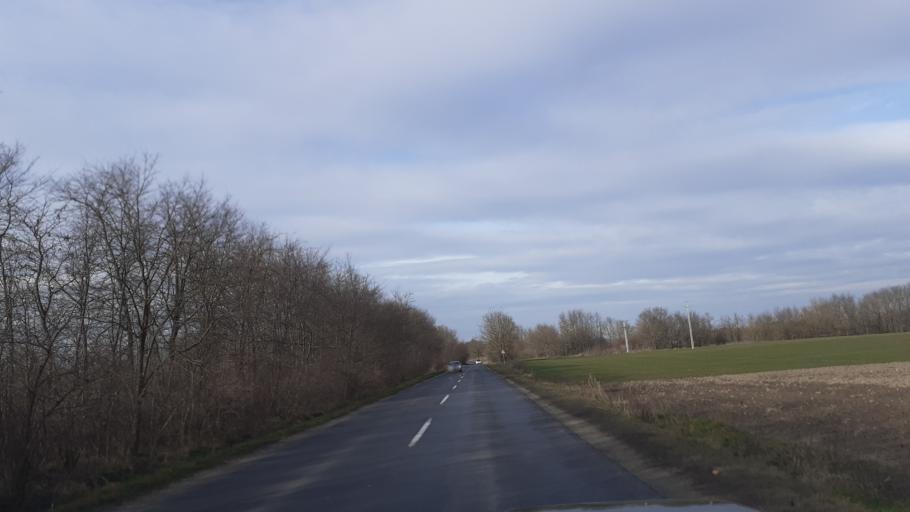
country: HU
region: Fejer
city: Kaloz
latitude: 46.9703
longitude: 18.4817
